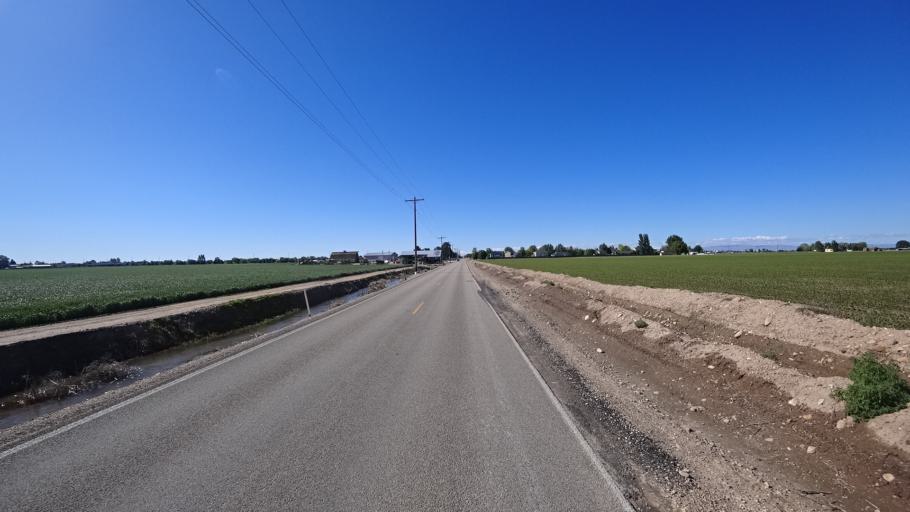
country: US
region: Idaho
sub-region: Ada County
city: Star
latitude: 43.6408
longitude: -116.4536
